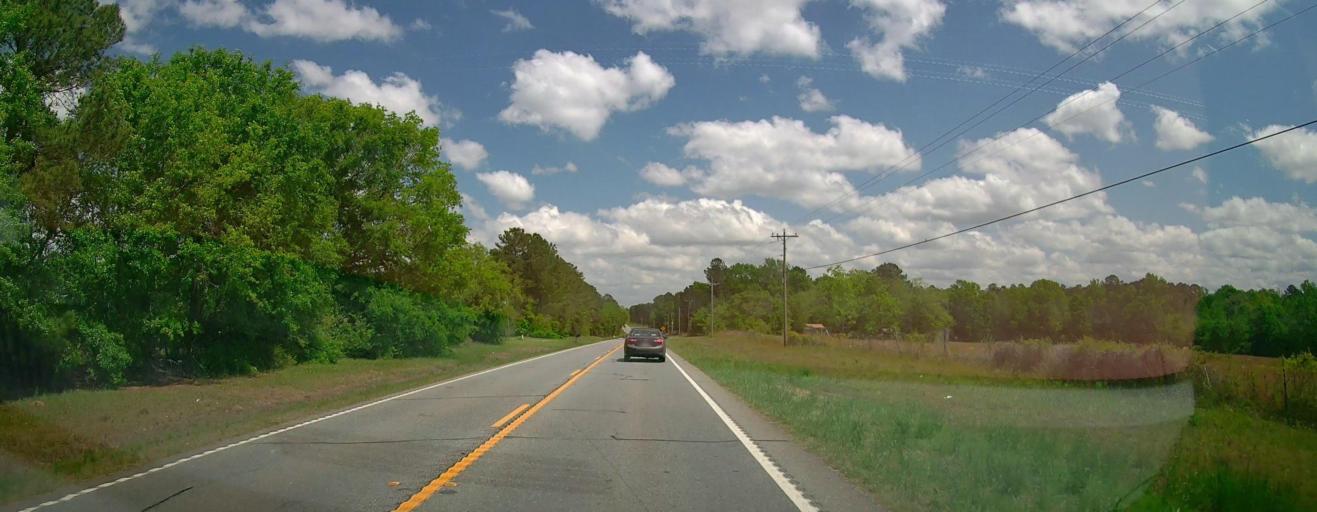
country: US
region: Georgia
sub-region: Bleckley County
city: Cochran
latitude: 32.4279
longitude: -83.3089
